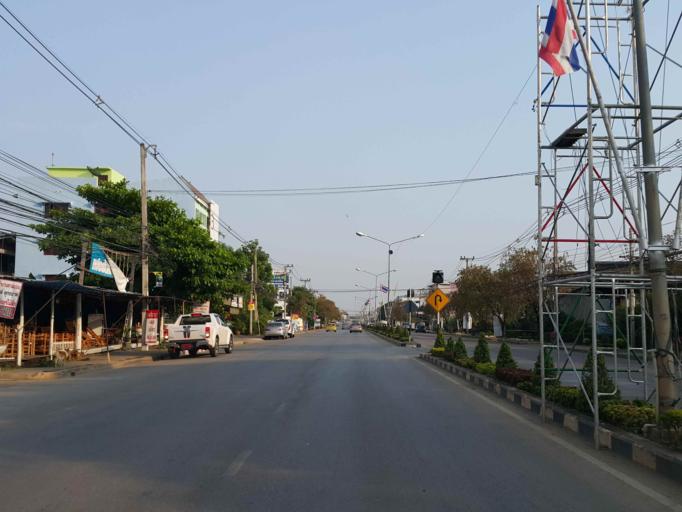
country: TH
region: Sukhothai
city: Sawankhalok
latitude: 17.3067
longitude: 99.8324
